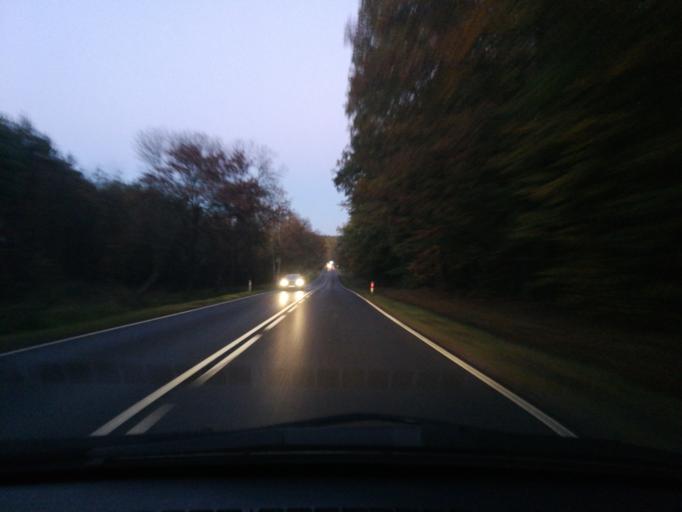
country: PL
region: Lodz Voivodeship
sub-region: Powiat brzezinski
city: Rogow
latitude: 51.8056
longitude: 19.8334
